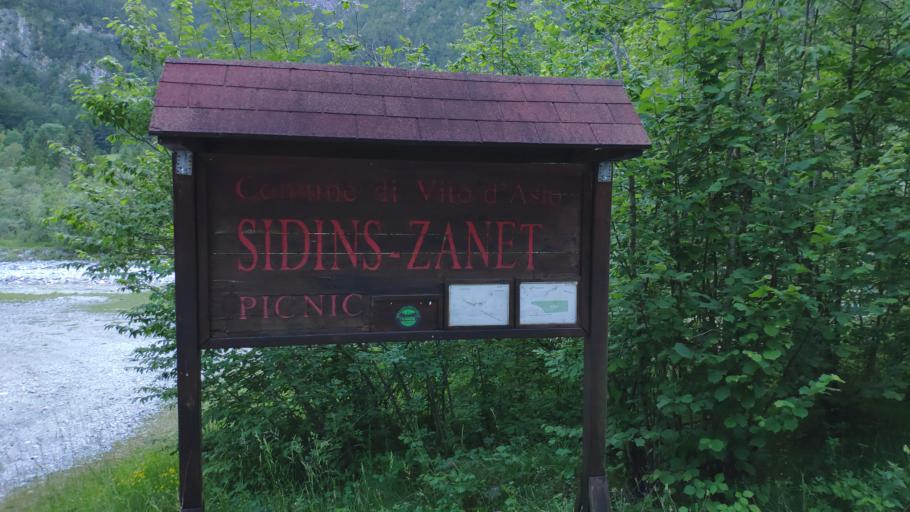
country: IT
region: Friuli Venezia Giulia
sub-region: Provincia di Pordenone
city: Anduins
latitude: 46.3045
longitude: 12.9315
